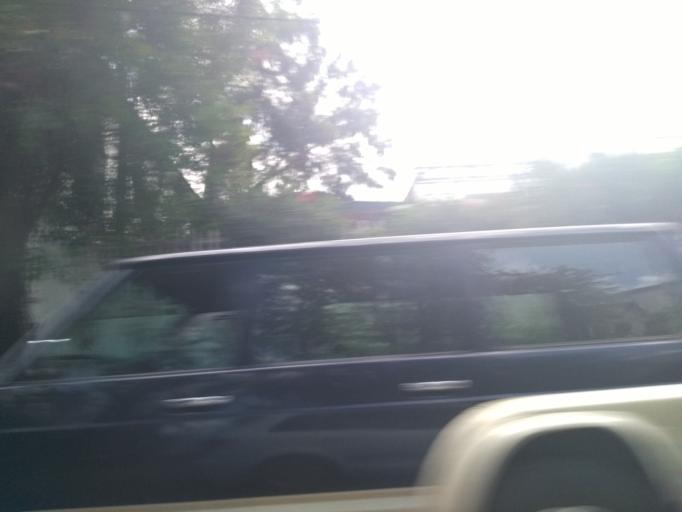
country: TZ
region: Dar es Salaam
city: Dar es Salaam
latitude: -6.8123
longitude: 39.2870
